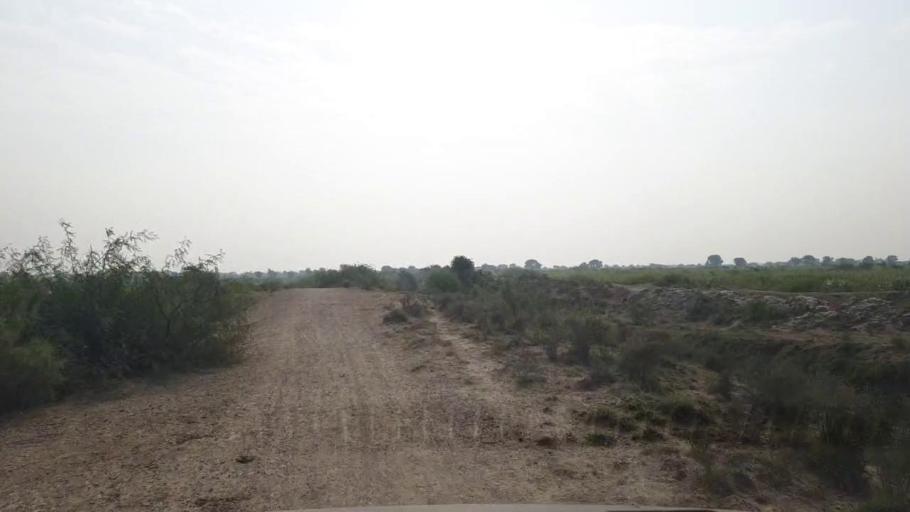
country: PK
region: Sindh
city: Tando Muhammad Khan
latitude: 25.1195
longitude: 68.4935
